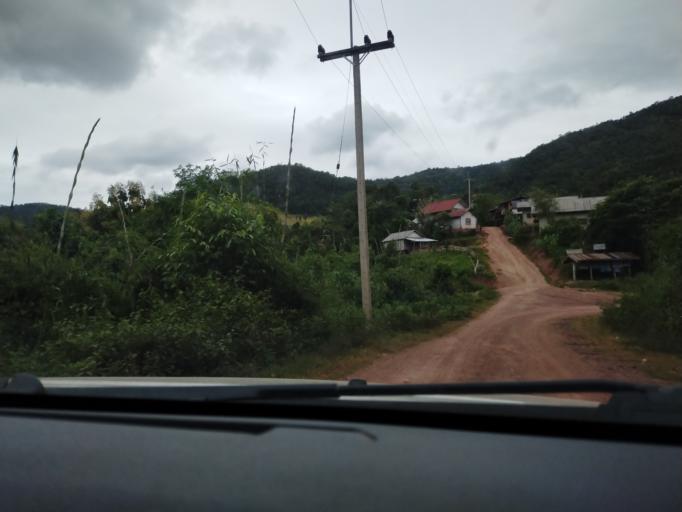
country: TH
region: Nan
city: Chaloem Phra Kiat
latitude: 19.7741
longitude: 101.3486
